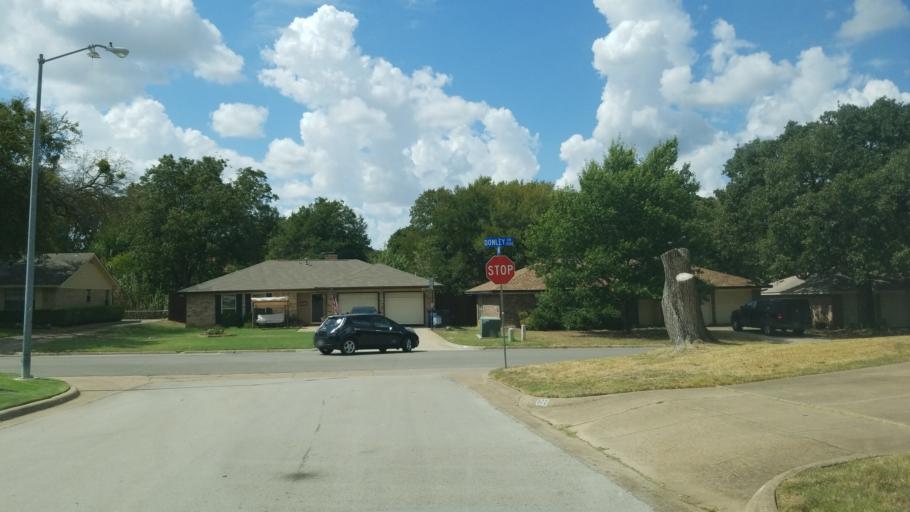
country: US
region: Texas
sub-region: Tarrant County
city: Euless
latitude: 32.8586
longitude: -97.0954
